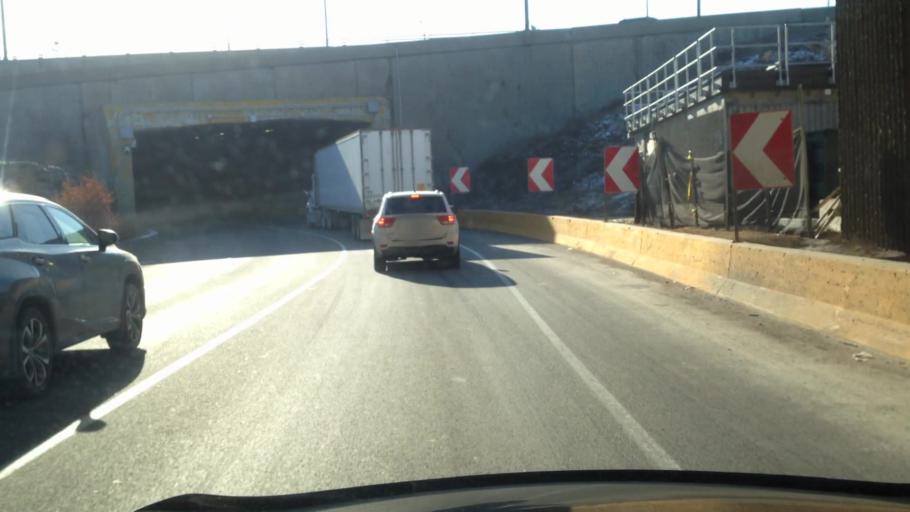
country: CA
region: Quebec
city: Cote-Saint-Luc
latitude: 45.4487
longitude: -73.6972
